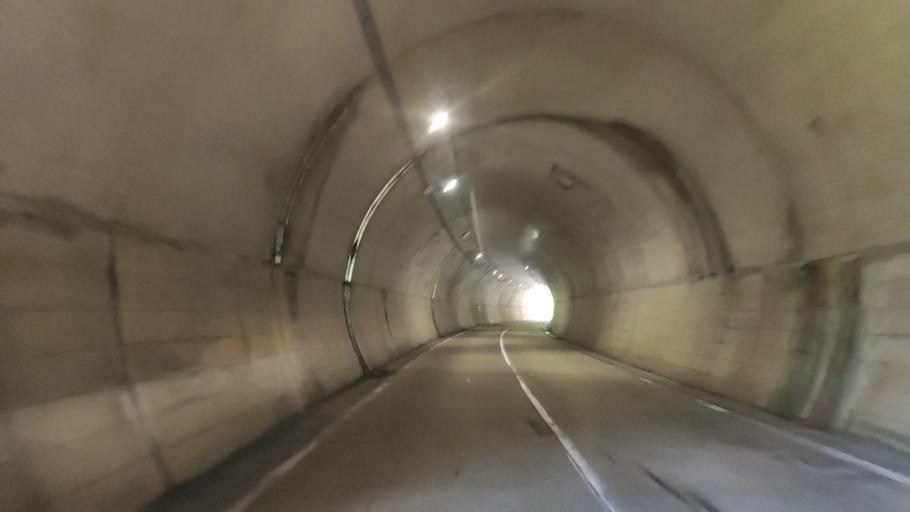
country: JP
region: Fukui
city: Ono
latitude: 35.8948
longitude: 136.5071
